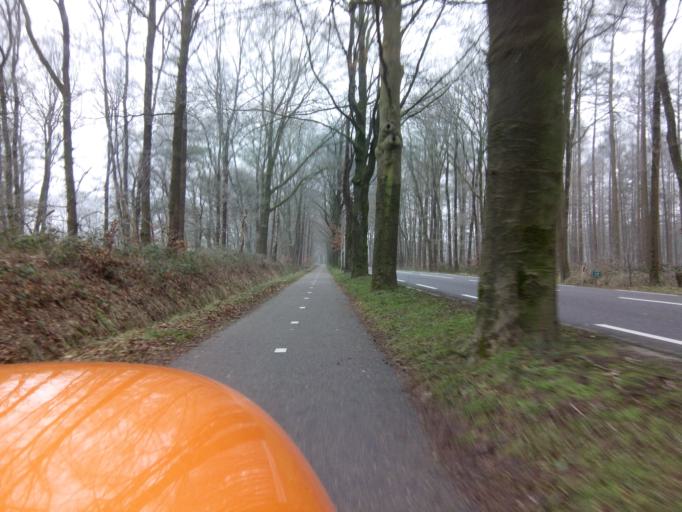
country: NL
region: Gelderland
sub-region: Gemeente Barneveld
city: Voorthuizen
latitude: 52.2070
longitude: 5.6080
